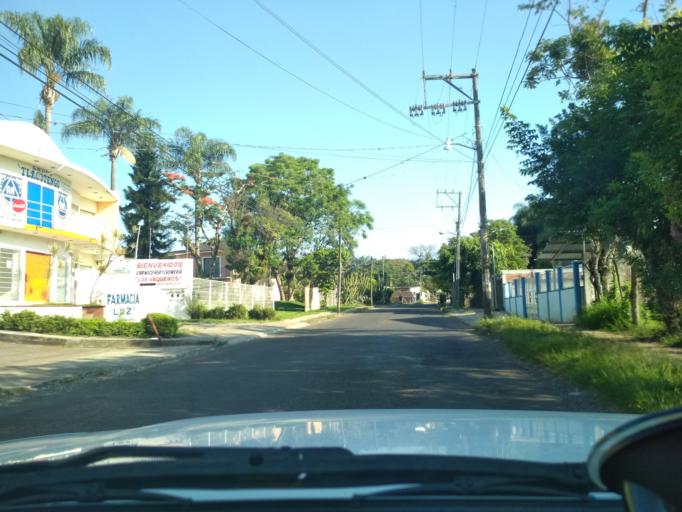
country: MX
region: Veracruz
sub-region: Fortin
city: Fraccionamiento Villas de la Llave
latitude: 18.9164
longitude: -96.9890
